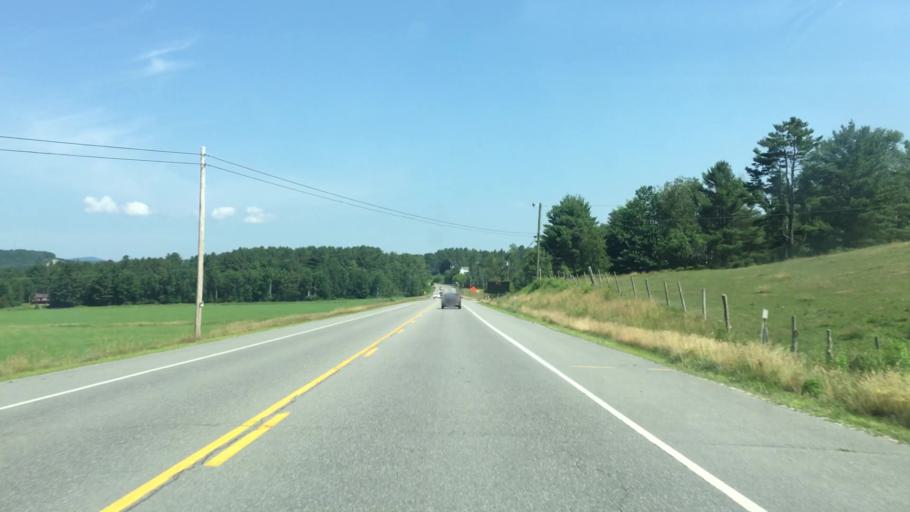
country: US
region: New Hampshire
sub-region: Sullivan County
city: Sunapee
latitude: 43.3636
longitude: -72.1204
